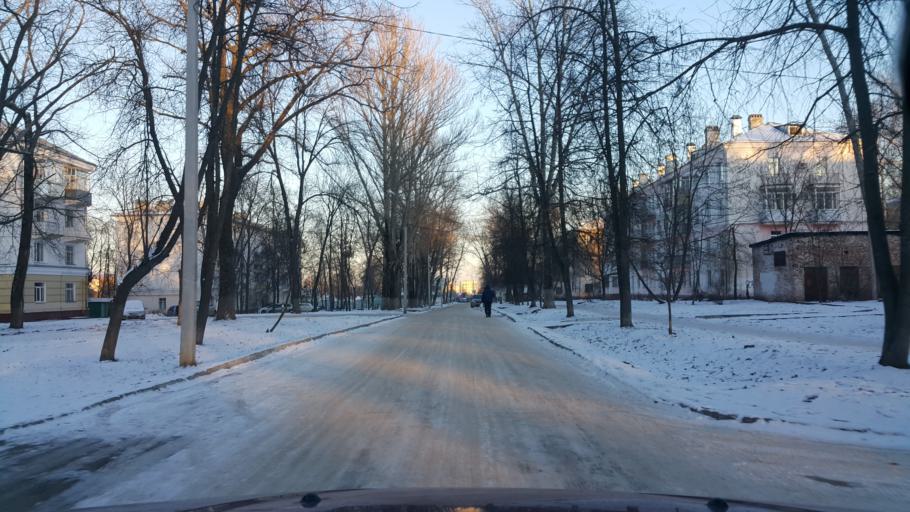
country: RU
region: Tambov
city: Pokrovo-Prigorodnoye
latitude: 52.7092
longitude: 41.3927
